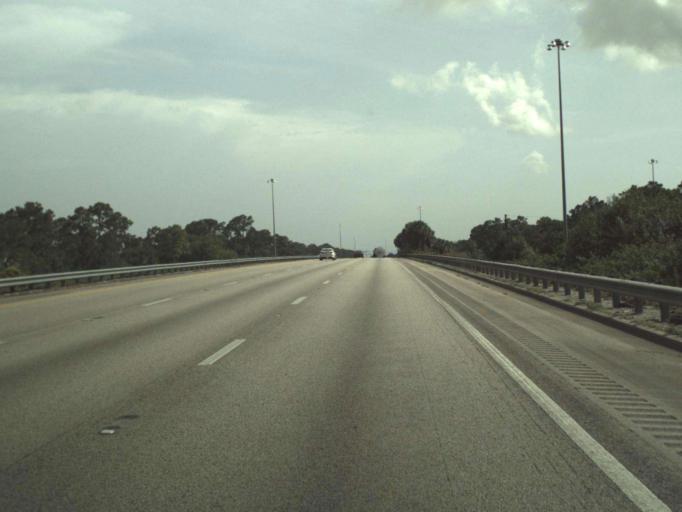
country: US
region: Florida
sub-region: Saint Lucie County
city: Fort Pierce South
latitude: 27.3766
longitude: -80.4093
